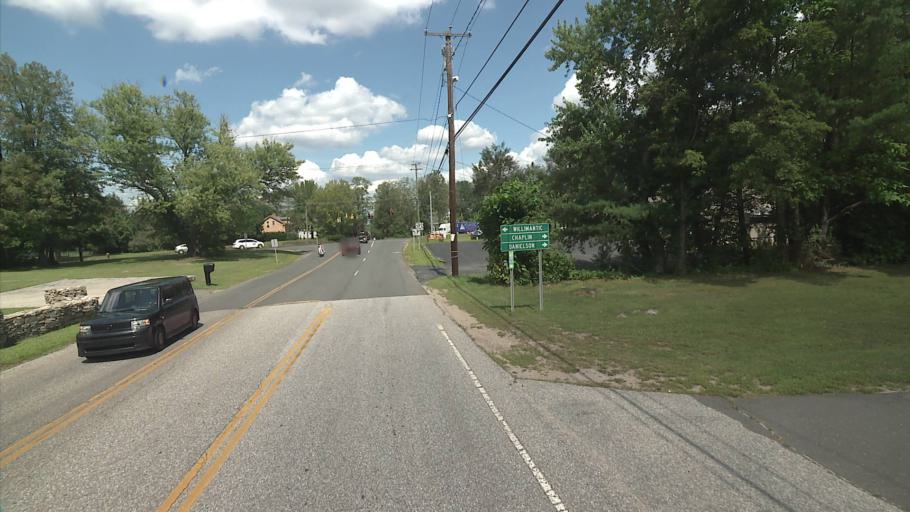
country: US
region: Connecticut
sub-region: Windham County
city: Windham
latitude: 41.7474
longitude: -72.1557
